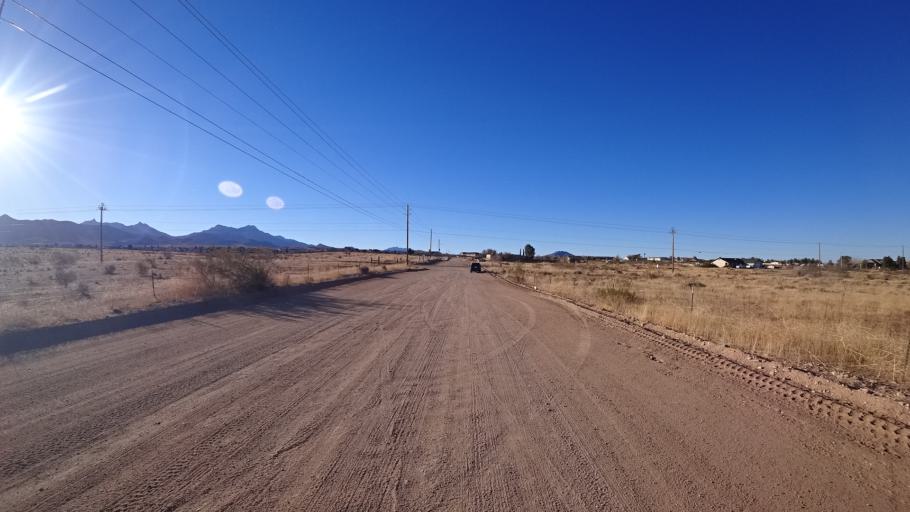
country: US
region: Arizona
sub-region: Mohave County
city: Kingman
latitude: 35.2002
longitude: -113.9939
